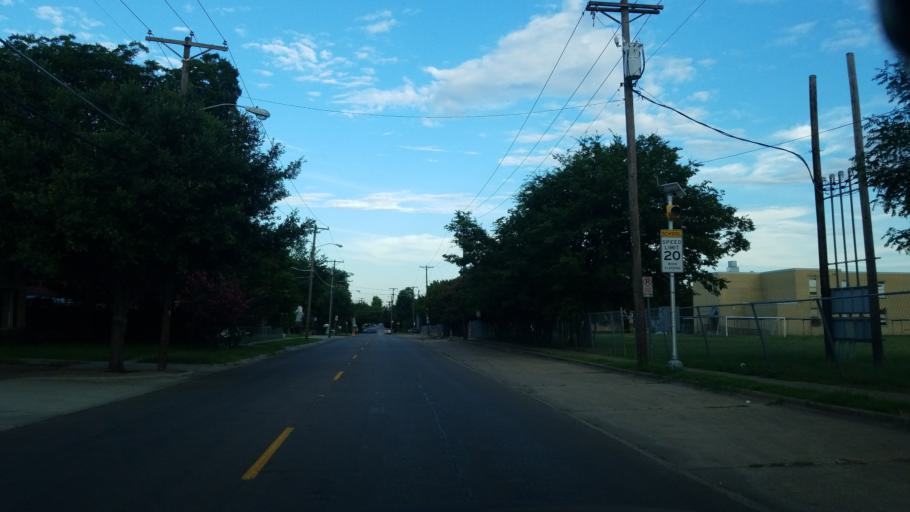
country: US
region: Texas
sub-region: Dallas County
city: Highland Park
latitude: 32.8092
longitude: -96.7878
